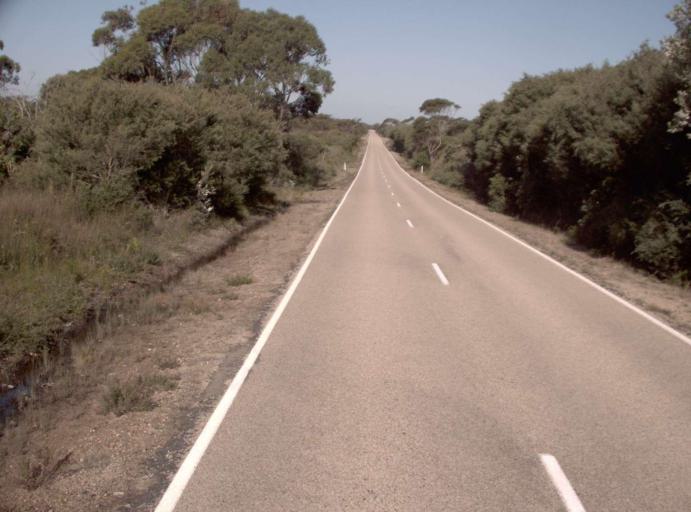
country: AU
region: Victoria
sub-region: East Gippsland
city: Lakes Entrance
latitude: -37.8011
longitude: 148.6415
